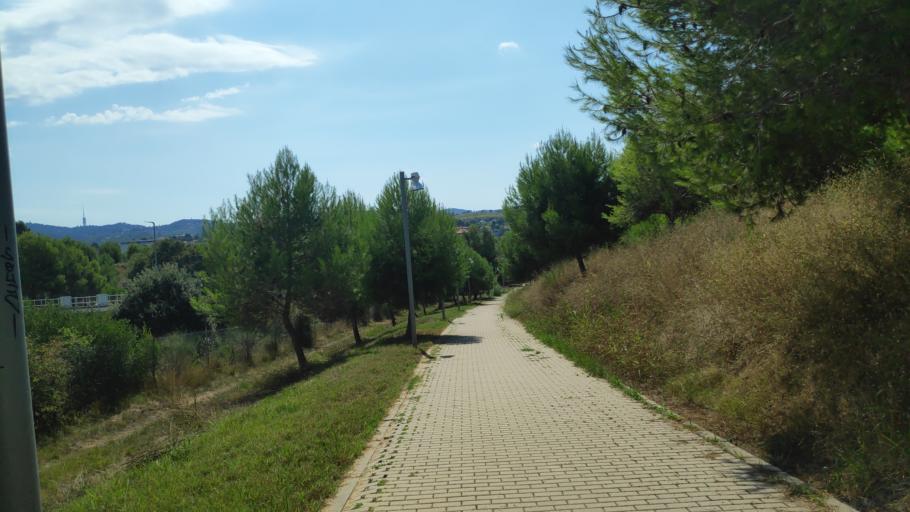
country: ES
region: Catalonia
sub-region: Provincia de Barcelona
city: Sant Cugat del Valles
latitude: 41.4722
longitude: 2.0643
